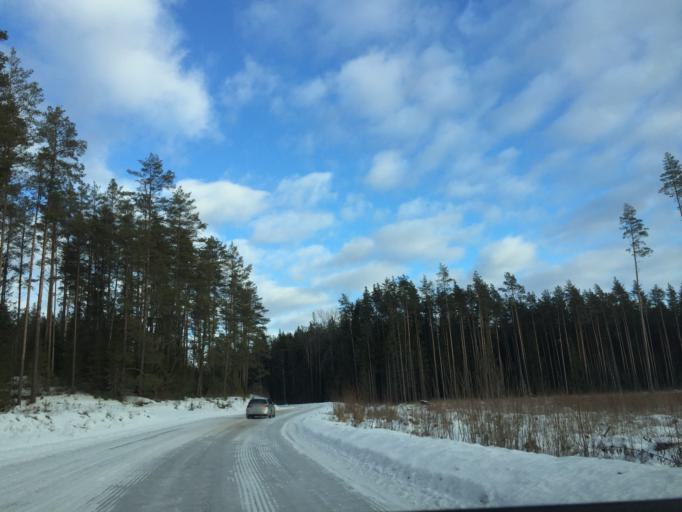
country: LV
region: Ogre
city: Jumprava
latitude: 56.5793
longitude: 24.9494
